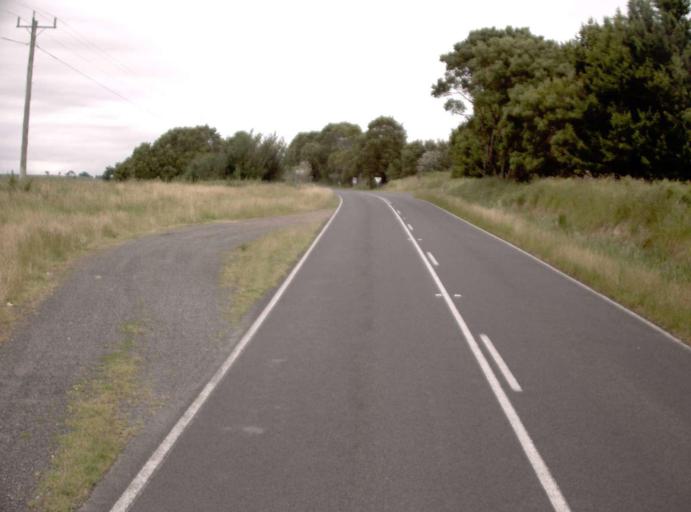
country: AU
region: Victoria
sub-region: Bass Coast
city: North Wonthaggi
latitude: -38.4651
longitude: 145.7802
